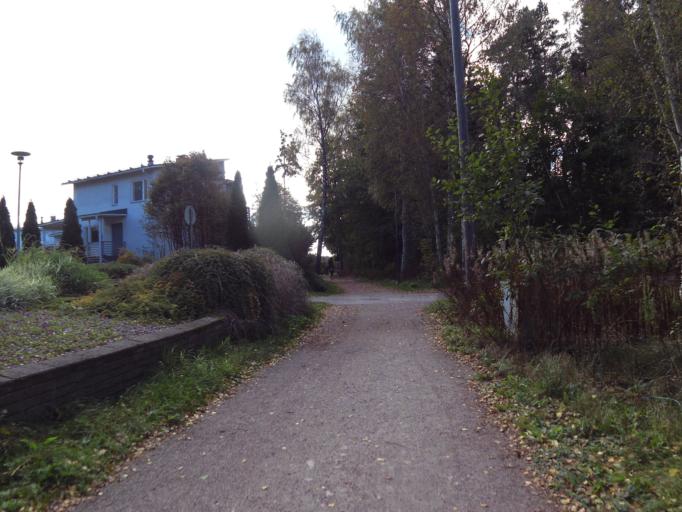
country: FI
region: Uusimaa
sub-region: Helsinki
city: Koukkuniemi
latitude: 60.1487
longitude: 24.7520
